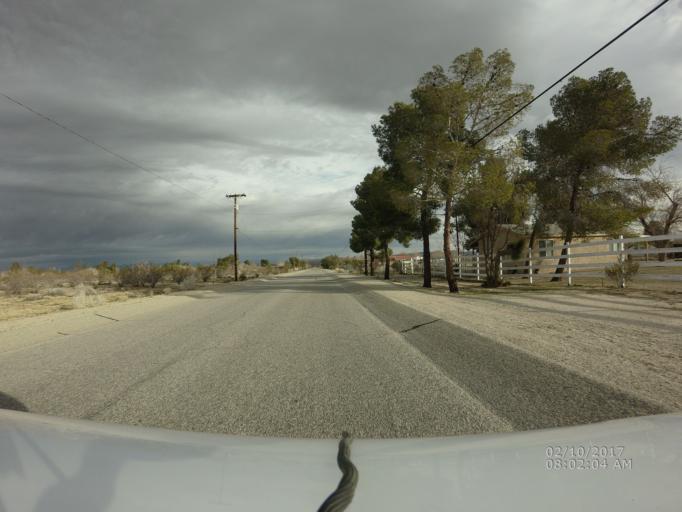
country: US
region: California
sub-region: Los Angeles County
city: Littlerock
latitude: 34.5016
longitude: -117.9054
